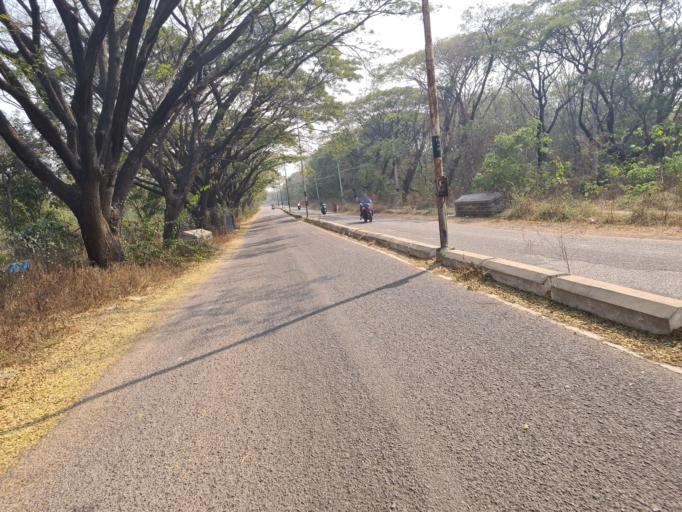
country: IN
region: Telangana
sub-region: Medak
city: Serilingampalle
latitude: 17.4890
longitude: 78.2979
